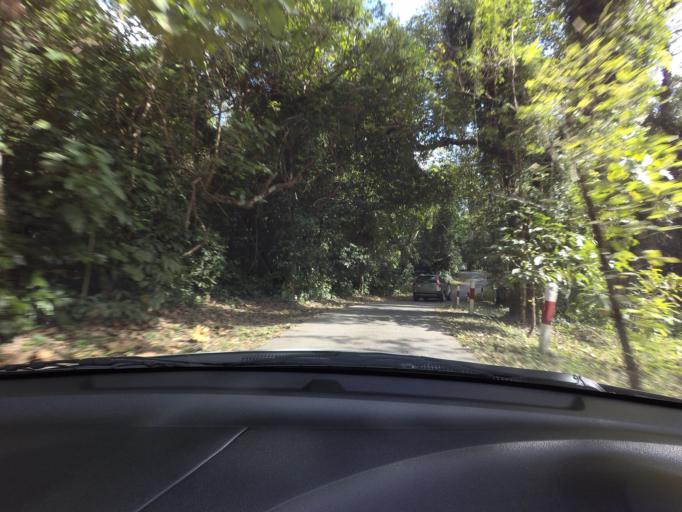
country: TH
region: Nakhon Nayok
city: Nakhon Nayok
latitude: 14.3274
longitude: 101.3074
